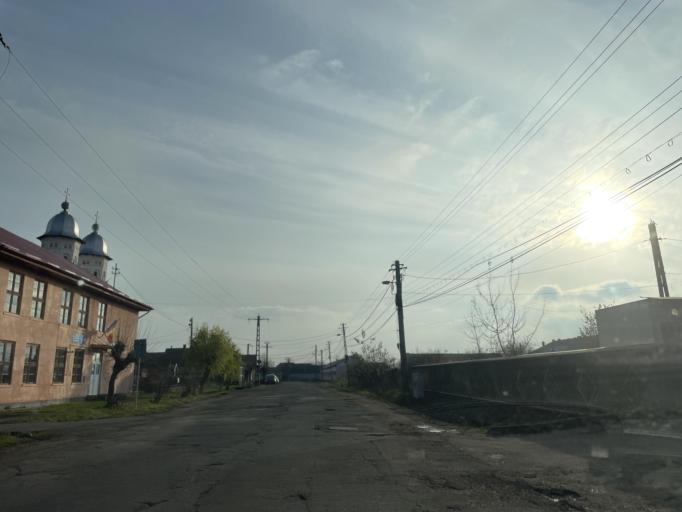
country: RO
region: Mures
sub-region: Municipiul Reghin
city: Apalina
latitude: 46.7532
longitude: 24.6932
